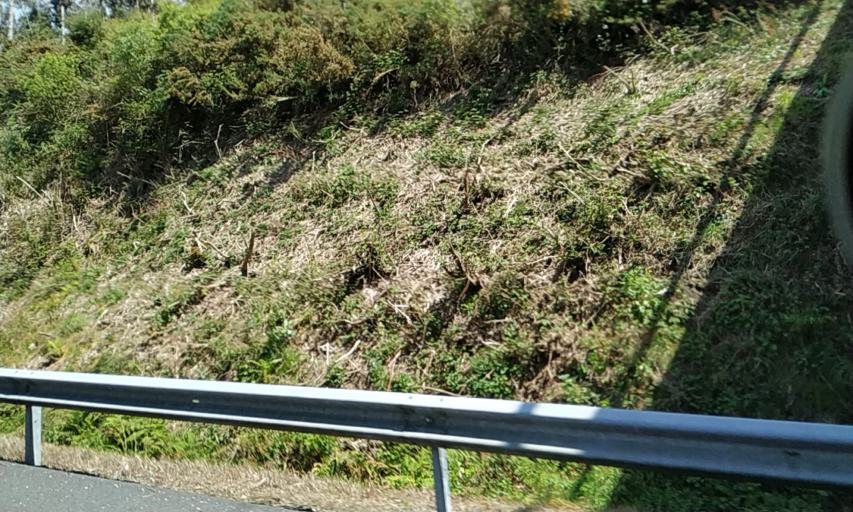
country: ES
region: Galicia
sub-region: Provincia da Coruna
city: Santiago de Compostela
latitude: 42.8355
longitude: -8.5728
